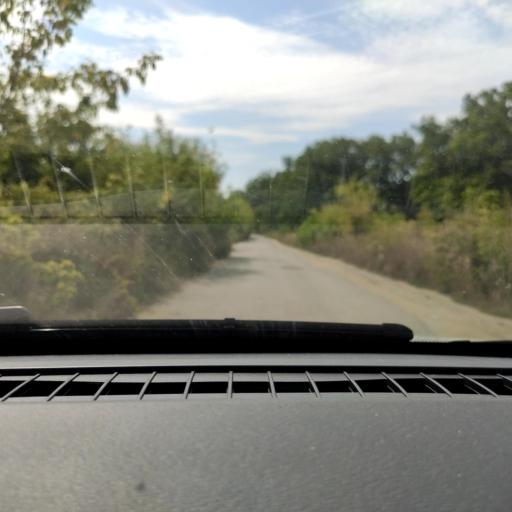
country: RU
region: Voronezj
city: Pridonskoy
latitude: 51.7467
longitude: 39.0745
